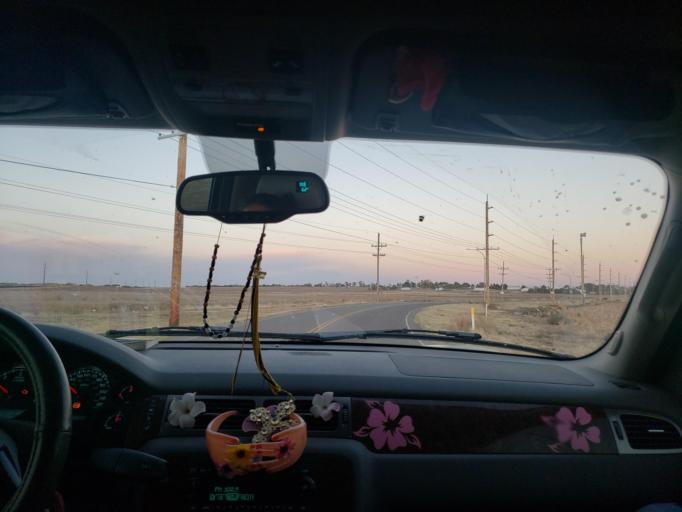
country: US
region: Kansas
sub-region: Finney County
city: Garden City
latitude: 37.9892
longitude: -100.8280
